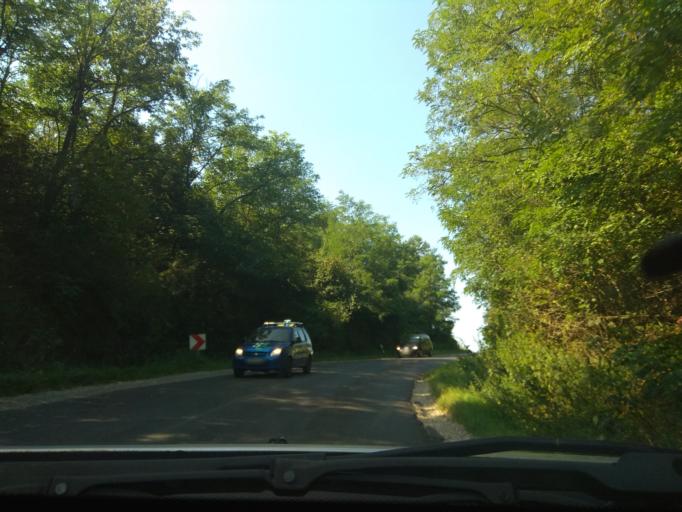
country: HU
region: Borsod-Abauj-Zemplen
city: Harsany
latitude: 47.9899
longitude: 20.7530
